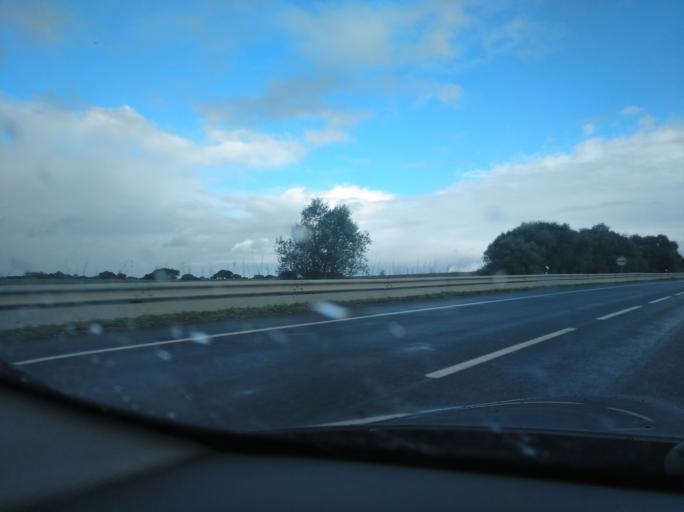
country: PT
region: Setubal
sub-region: Grandola
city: Grandola
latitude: 38.0110
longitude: -8.3818
